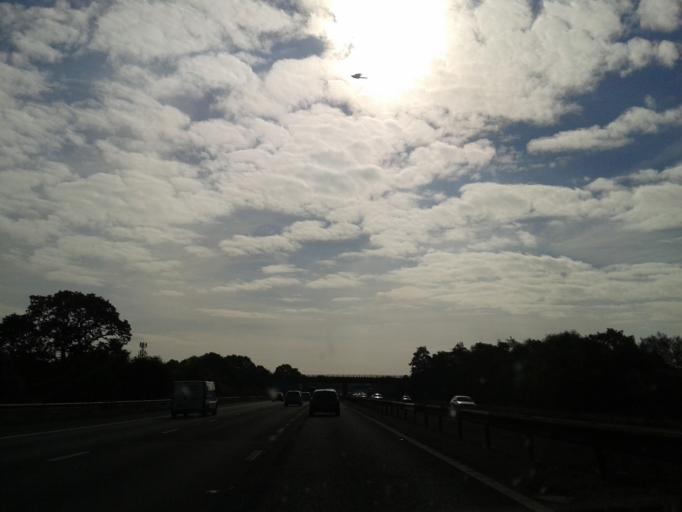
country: GB
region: England
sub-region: Cheshire East
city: Holmes Chapel
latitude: 53.1890
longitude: -2.3775
